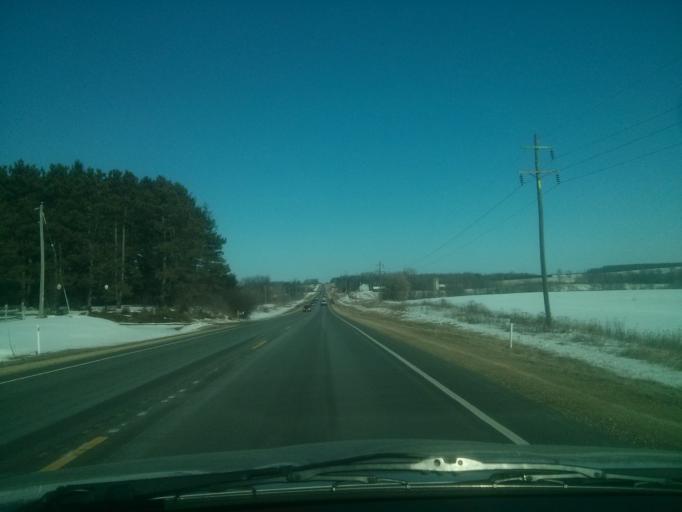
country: US
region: Wisconsin
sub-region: Polk County
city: Clear Lake
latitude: 45.1424
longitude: -92.2818
